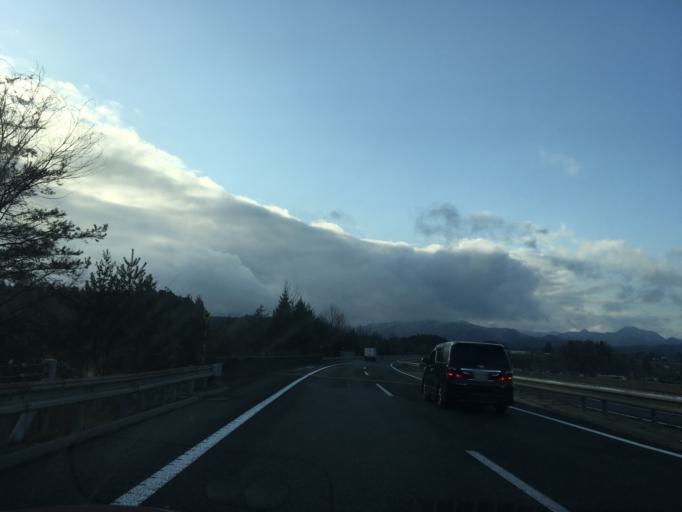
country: JP
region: Miyagi
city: Okawara
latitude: 38.1660
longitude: 140.6420
